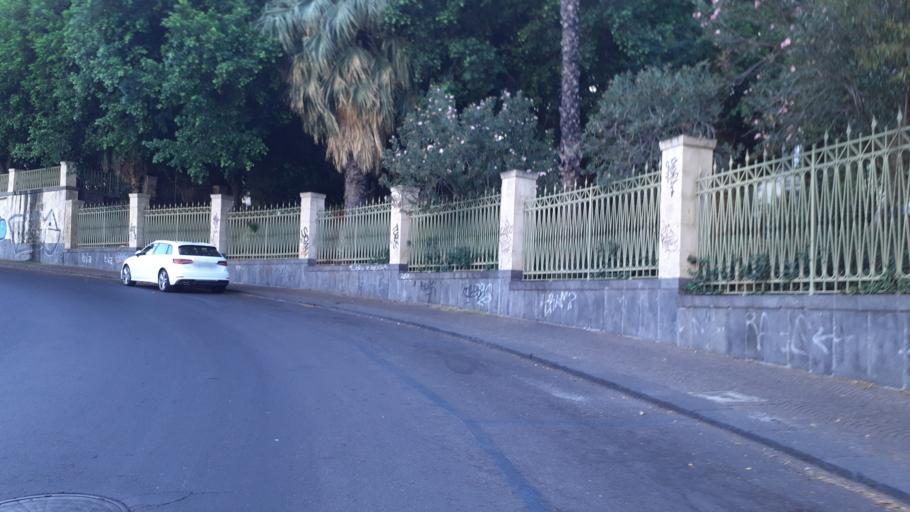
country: IT
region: Sicily
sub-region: Catania
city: Catania
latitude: 37.5097
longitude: 15.0836
